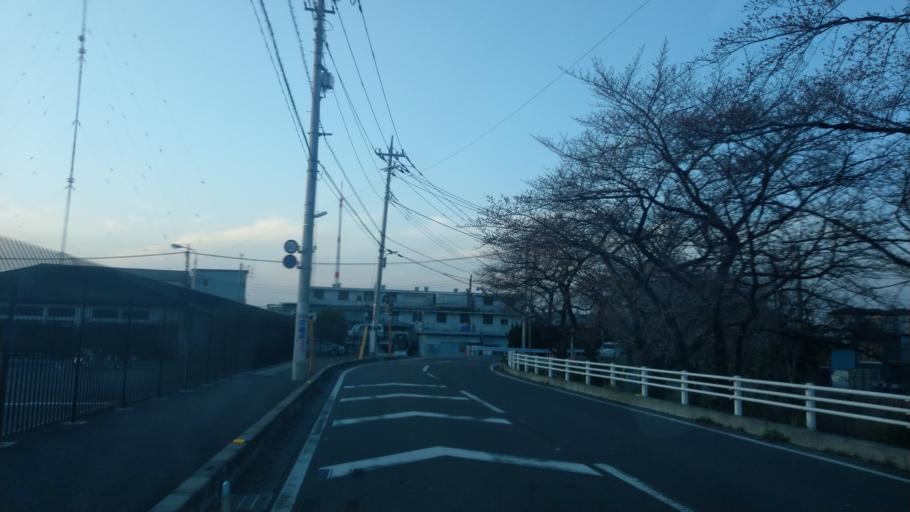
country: JP
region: Saitama
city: Shiki
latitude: 35.8460
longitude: 139.6185
